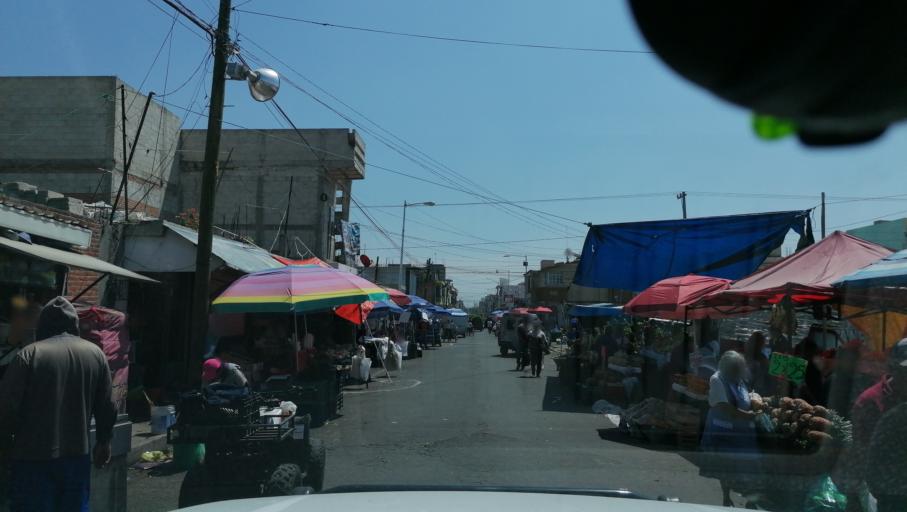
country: MX
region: Puebla
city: Huejotzingo
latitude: 19.1579
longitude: -98.4130
